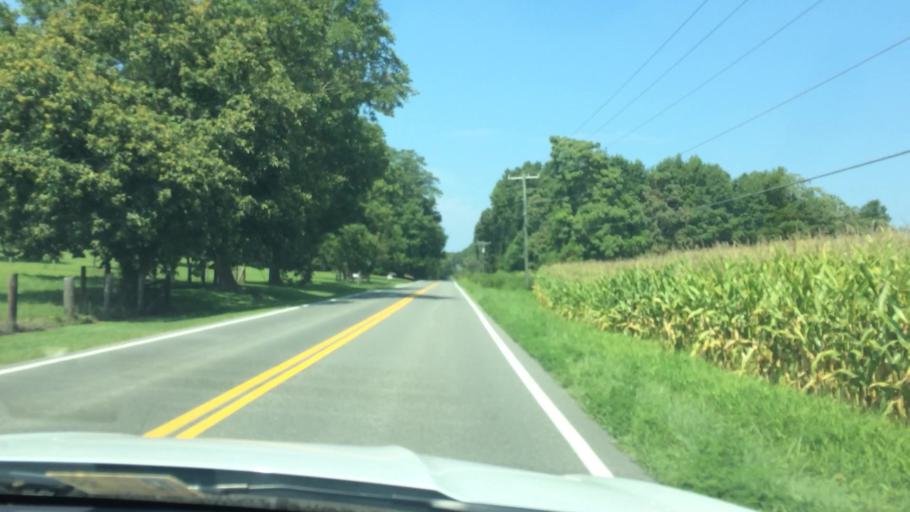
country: US
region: Virginia
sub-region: New Kent County
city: New Kent
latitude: 37.5253
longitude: -77.0135
